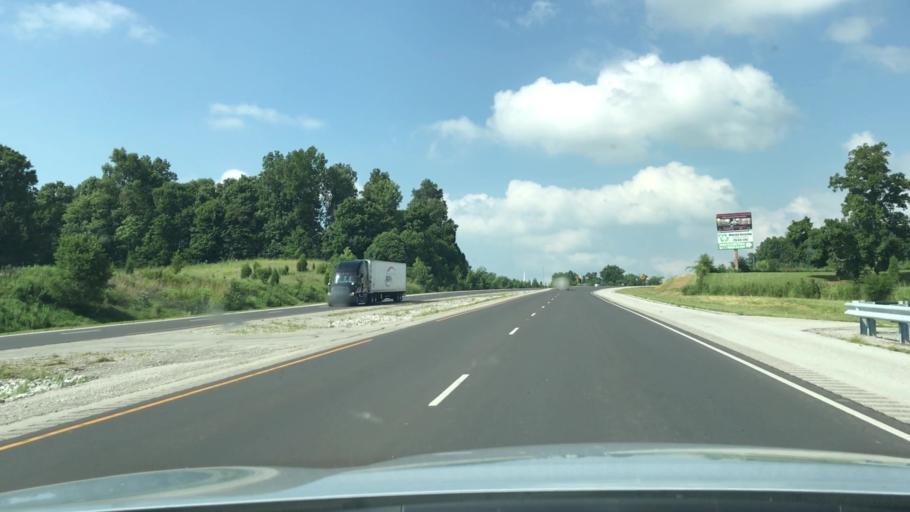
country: US
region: Kentucky
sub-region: Barren County
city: Glasgow
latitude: 37.0176
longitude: -85.9453
